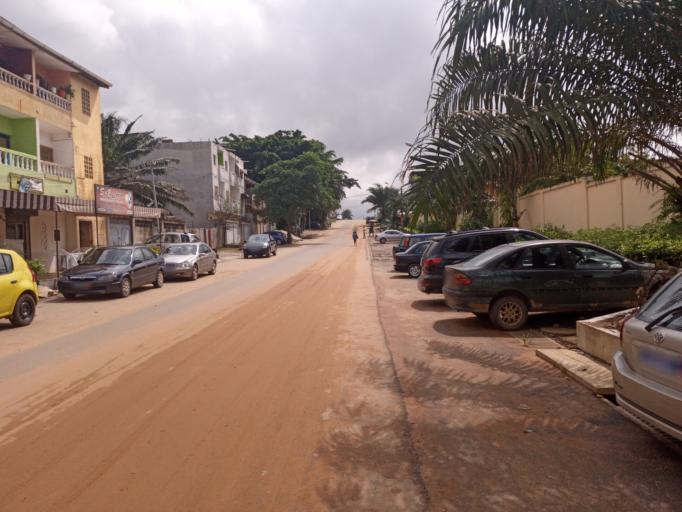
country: CI
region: Lagunes
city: Bingerville
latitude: 5.3645
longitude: -3.9564
